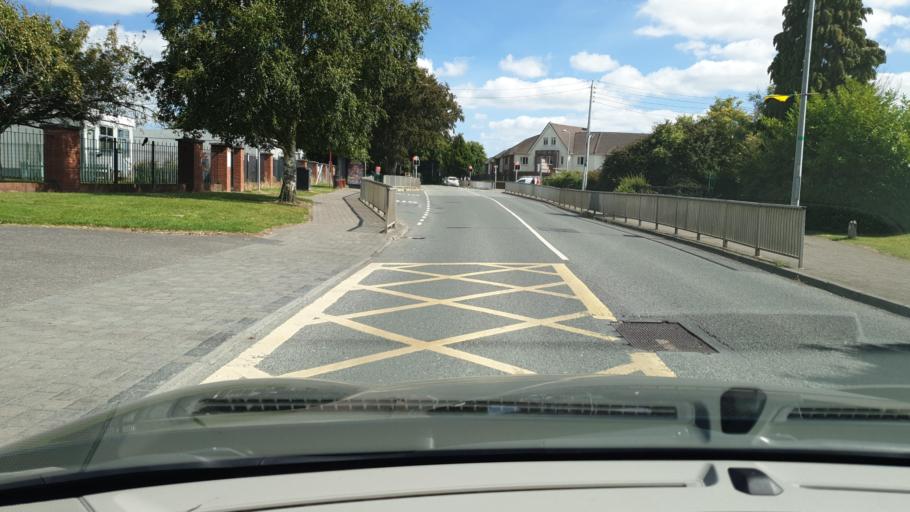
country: IE
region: Leinster
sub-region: An Mhi
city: Dunboyne
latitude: 53.4182
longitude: -6.4722
